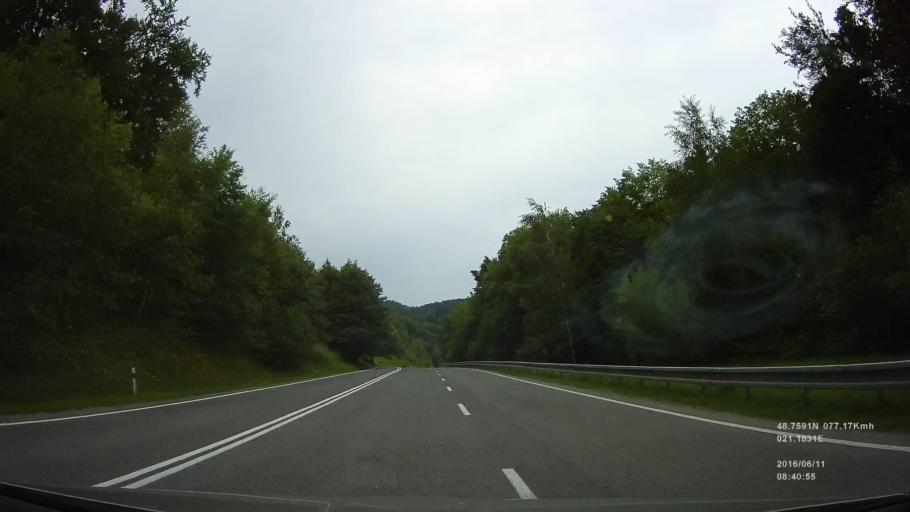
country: SK
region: Kosicky
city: Kosice
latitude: 48.7431
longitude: 21.2386
